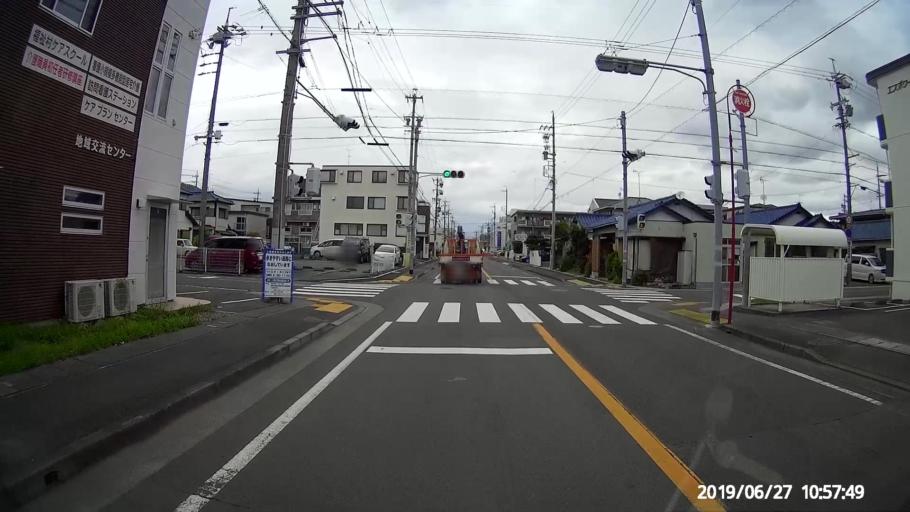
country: JP
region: Shizuoka
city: Shizuoka-shi
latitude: 34.9383
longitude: 138.3668
